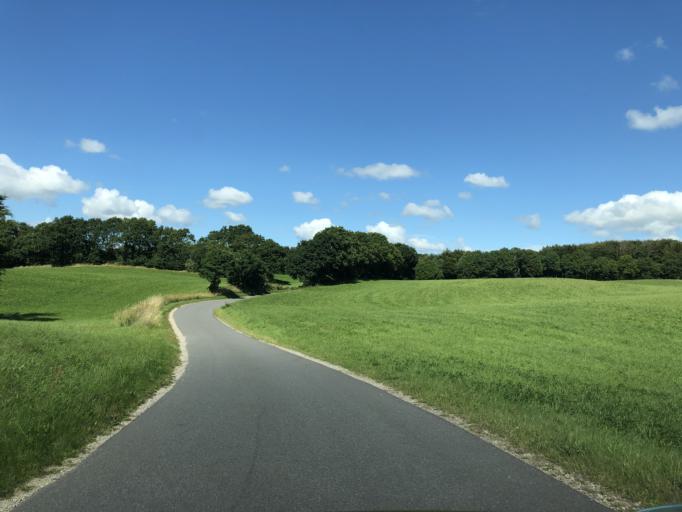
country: DK
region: Central Jutland
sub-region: Viborg Kommune
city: Stoholm
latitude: 56.4417
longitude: 9.1345
